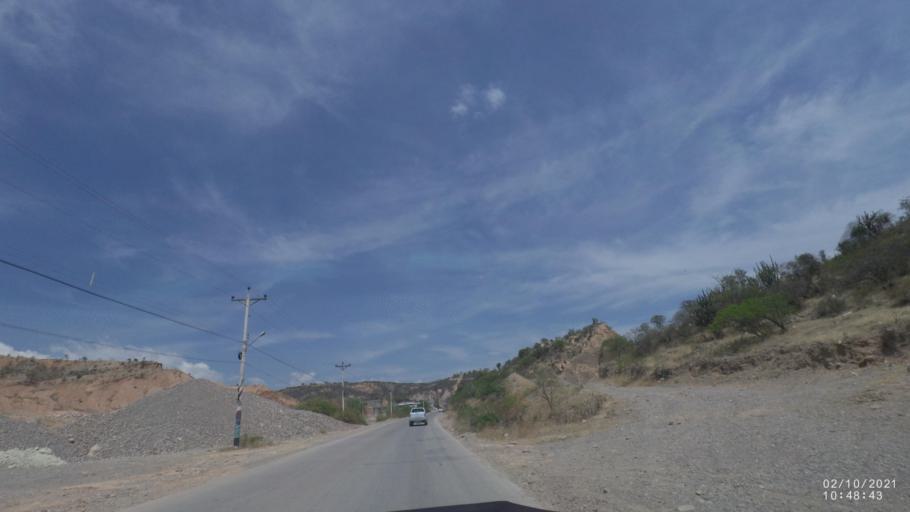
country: BO
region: Cochabamba
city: Sipe Sipe
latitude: -17.5795
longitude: -66.3374
